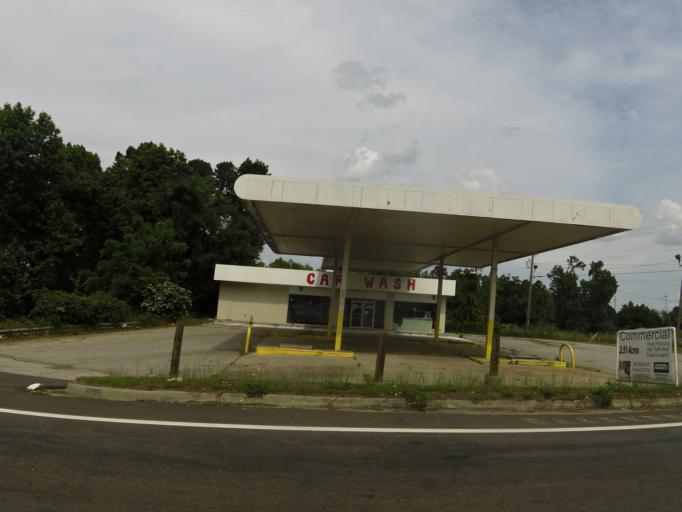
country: US
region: Georgia
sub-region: McDuffie County
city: Thomson
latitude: 33.5131
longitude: -82.5023
